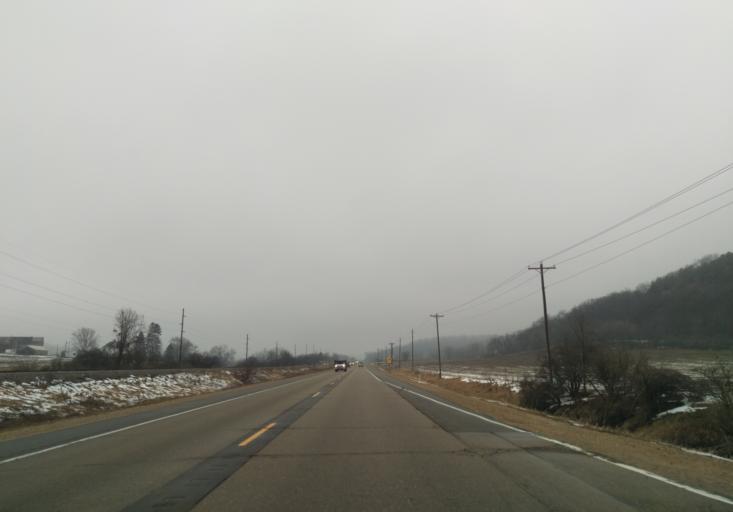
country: US
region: Wisconsin
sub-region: Dane County
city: Cross Plains
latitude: 43.0941
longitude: -89.6059
